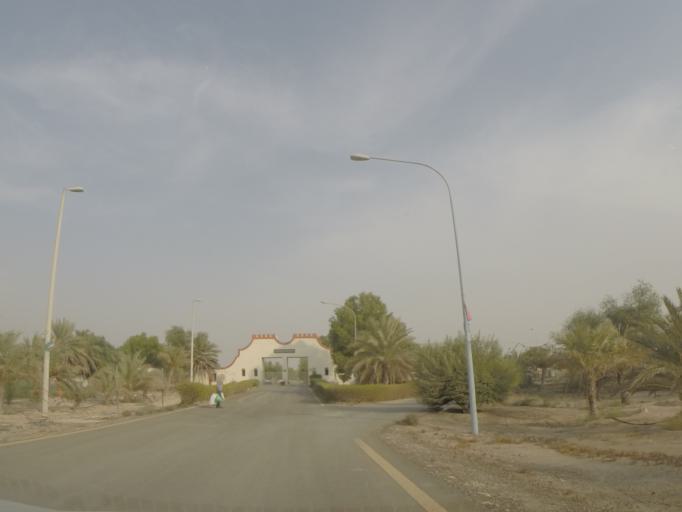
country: AE
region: Abu Dhabi
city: Abu Dhabi
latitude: 24.7038
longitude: 54.7904
